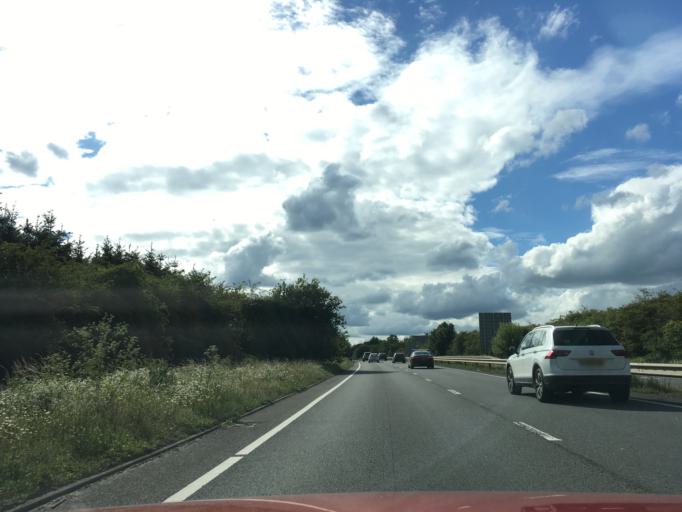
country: GB
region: England
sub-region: Oxfordshire
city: Wheatley
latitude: 51.7460
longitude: -1.1182
